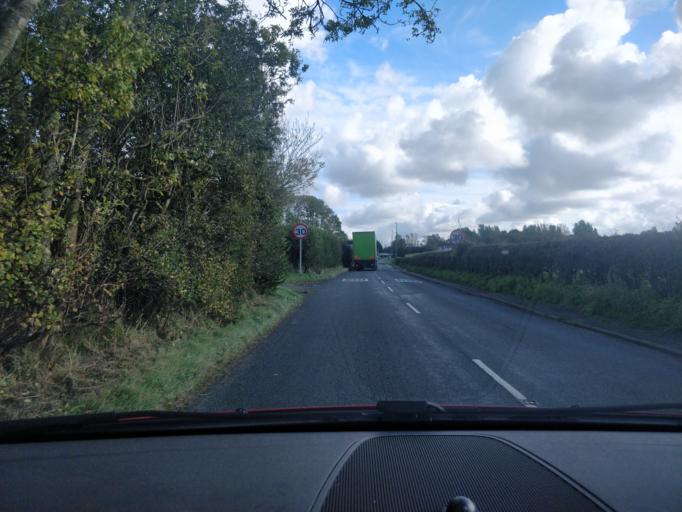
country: GB
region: England
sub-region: Lancashire
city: Ormskirk
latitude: 53.5881
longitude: -2.8686
